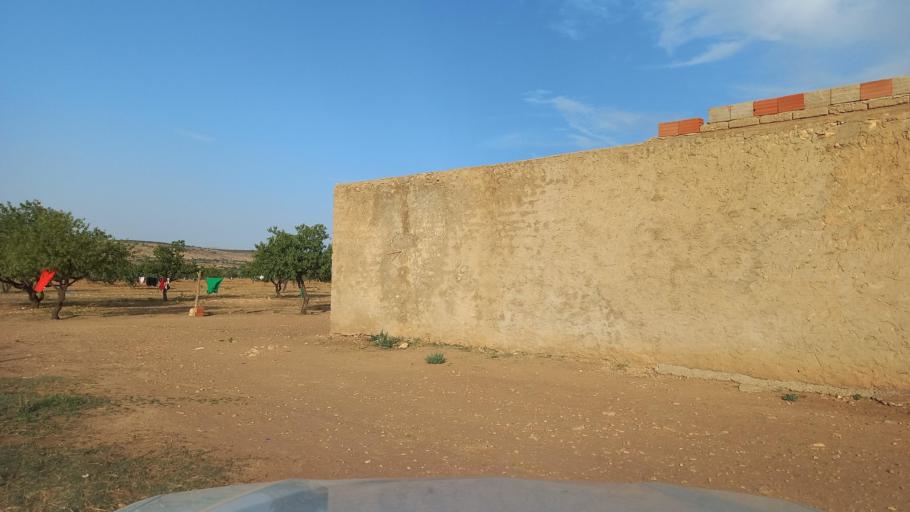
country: TN
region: Al Qasrayn
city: Kasserine
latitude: 35.3525
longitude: 8.8438
